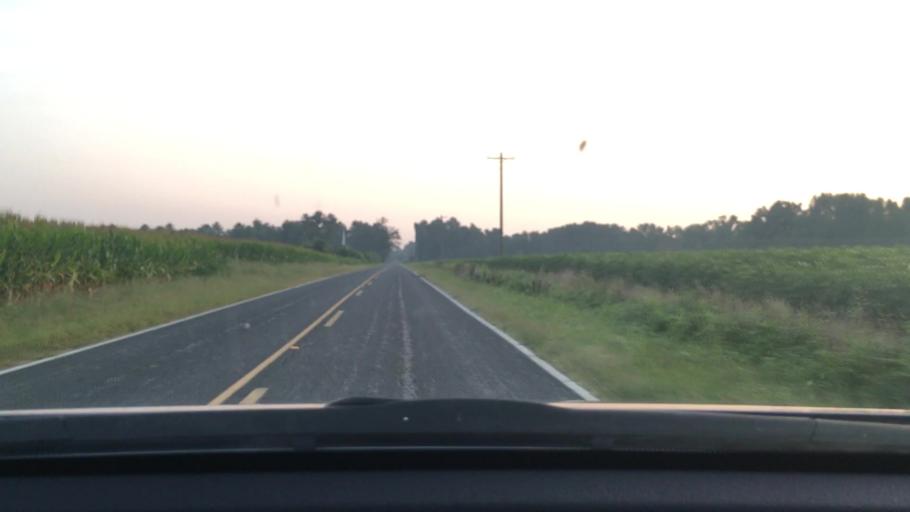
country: US
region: South Carolina
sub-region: Lee County
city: Bishopville
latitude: 34.1829
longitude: -80.1430
